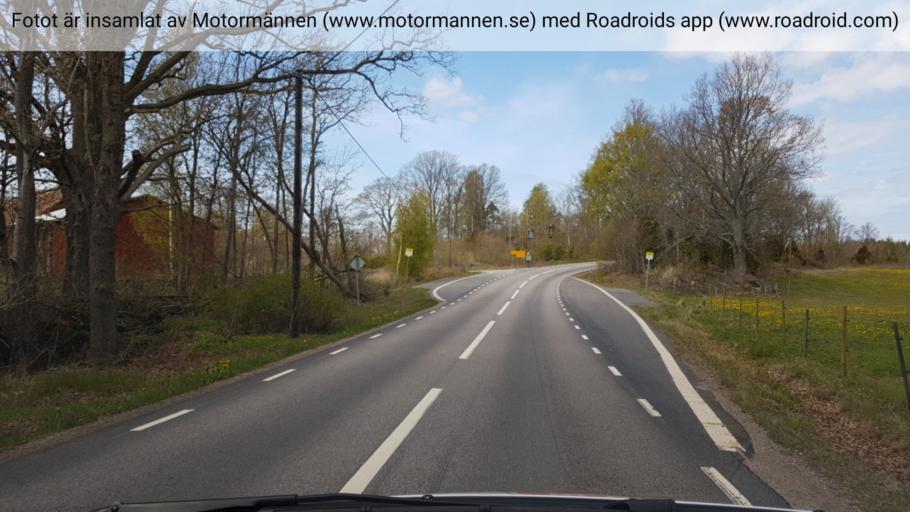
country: SE
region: Kalmar
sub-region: Vasterviks Kommun
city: Vaestervik
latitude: 57.9056
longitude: 16.6660
